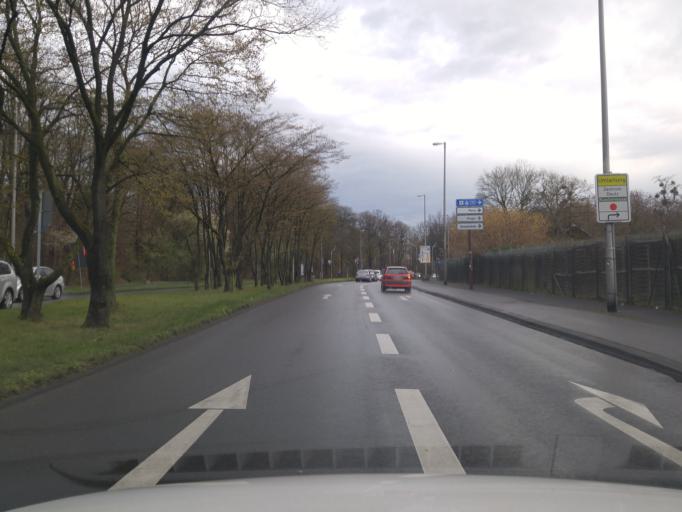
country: DE
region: North Rhine-Westphalia
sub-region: Regierungsbezirk Koln
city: Hoehenberg
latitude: 50.9396
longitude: 7.0321
